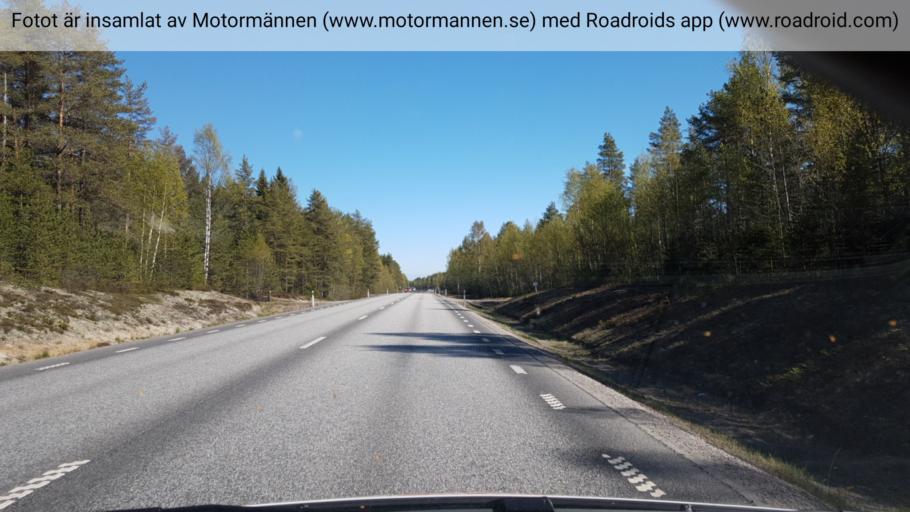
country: SE
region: Vaesterbotten
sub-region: Umea Kommun
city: Roback
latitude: 63.8528
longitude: 20.1066
